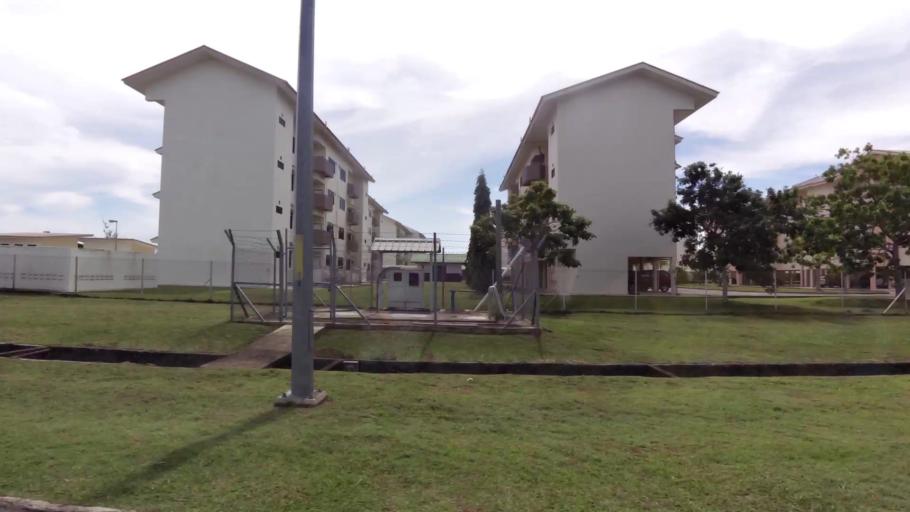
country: BN
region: Belait
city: Seria
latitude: 4.6018
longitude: 114.3141
